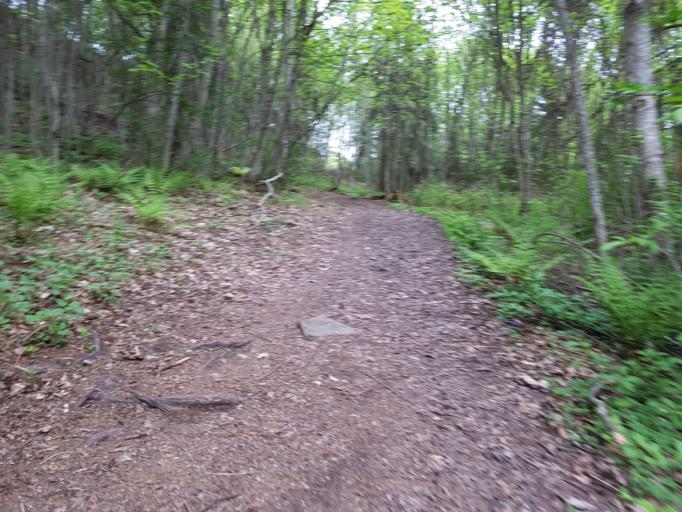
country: NO
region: Nord-Trondelag
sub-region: Levanger
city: Levanger
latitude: 63.7400
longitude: 11.2628
